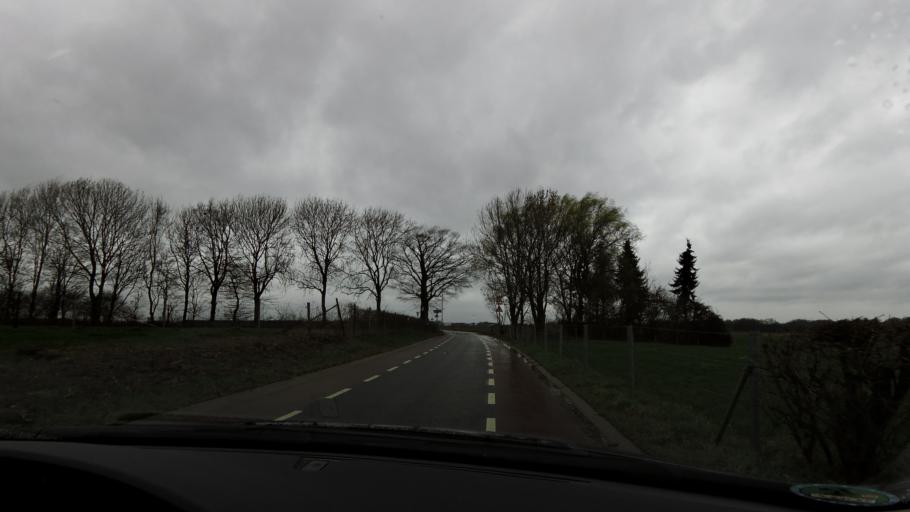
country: NL
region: Limburg
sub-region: Gemeente Beek
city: Beek
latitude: 50.9133
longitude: 5.8032
